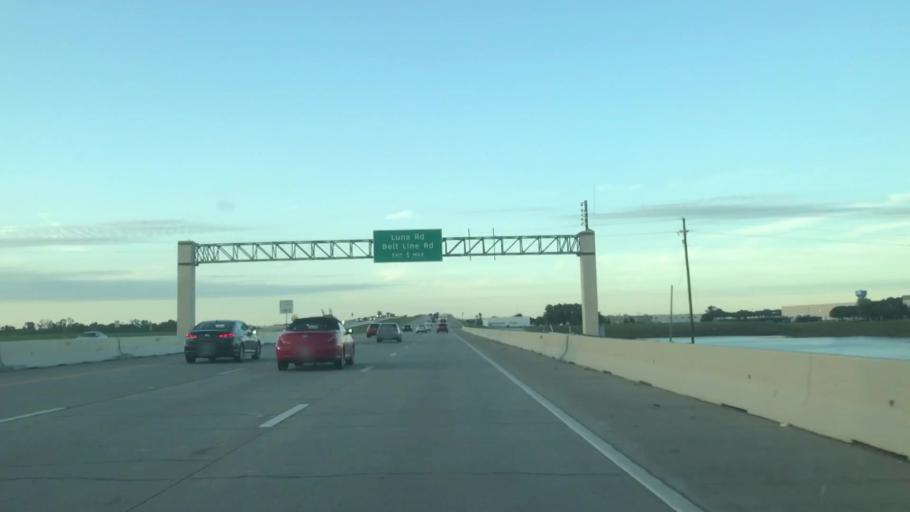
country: US
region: Texas
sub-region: Dallas County
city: Farmers Branch
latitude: 32.9303
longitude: -96.9304
